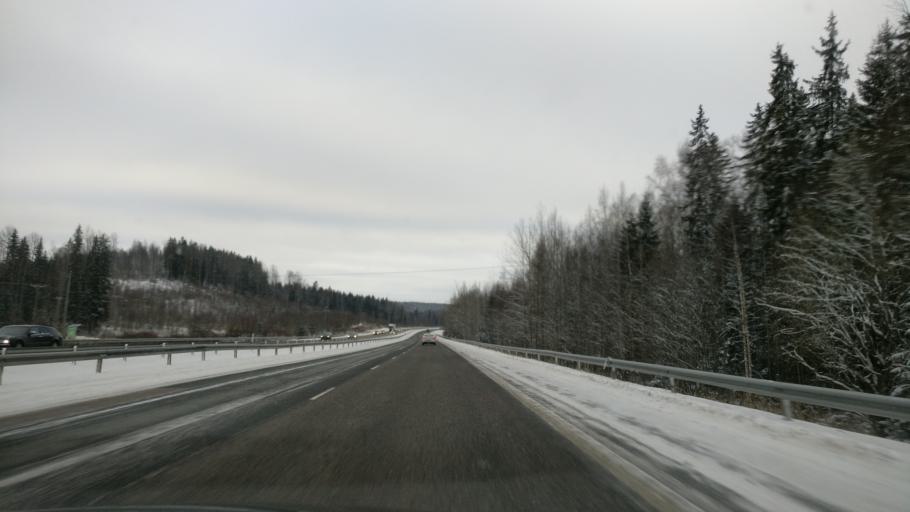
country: FI
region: Paijanne Tavastia
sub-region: Lahti
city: Lahti
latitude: 60.9573
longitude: 25.6977
